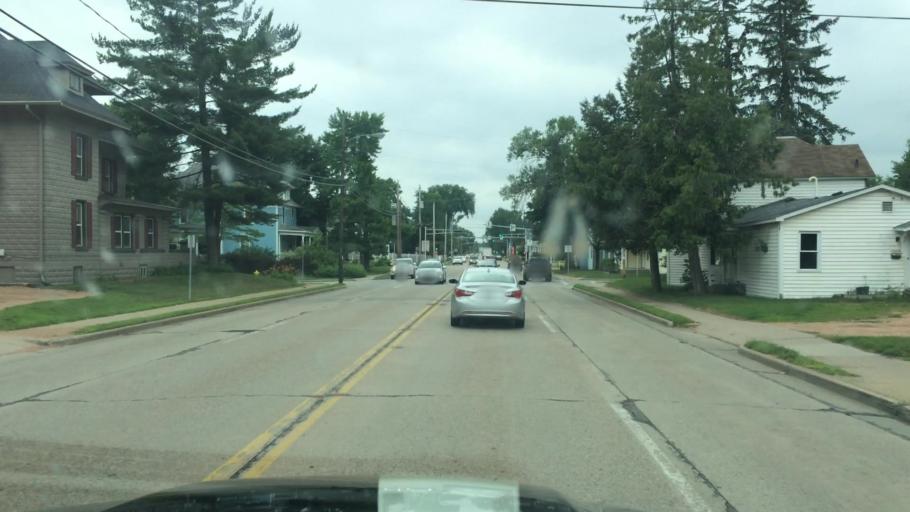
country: US
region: Wisconsin
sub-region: Portage County
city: Stevens Point
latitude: 44.5249
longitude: -89.5748
